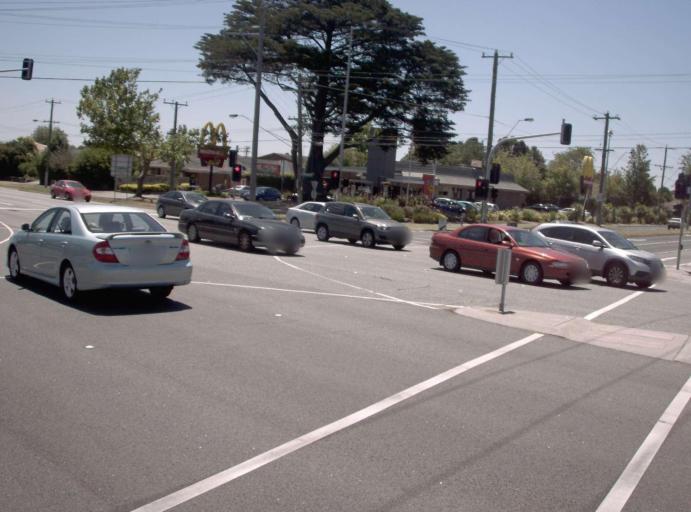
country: AU
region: Victoria
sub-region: Glen Eira
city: Murrumbeena
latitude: -37.8873
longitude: 145.0783
